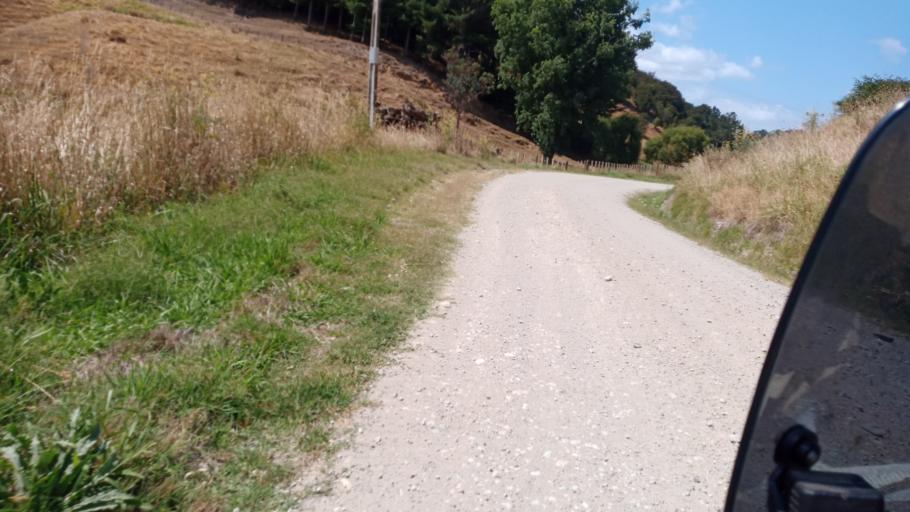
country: NZ
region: Gisborne
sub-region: Gisborne District
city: Gisborne
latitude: -38.4917
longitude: 177.8496
